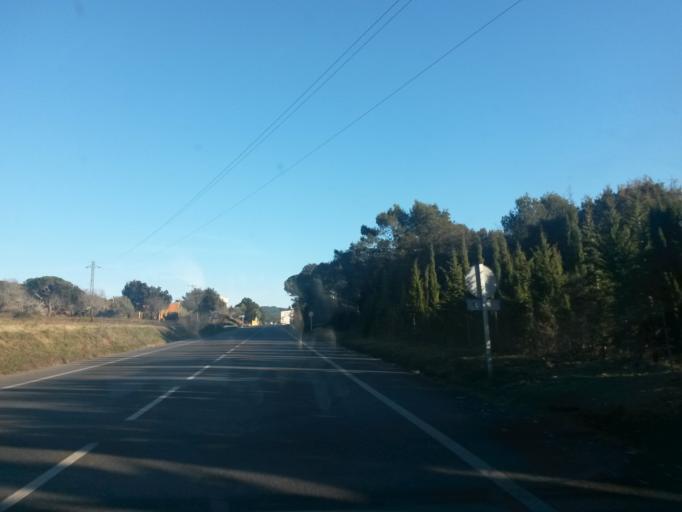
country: ES
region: Catalonia
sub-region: Provincia de Girona
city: Regencos
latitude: 41.9521
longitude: 3.1631
